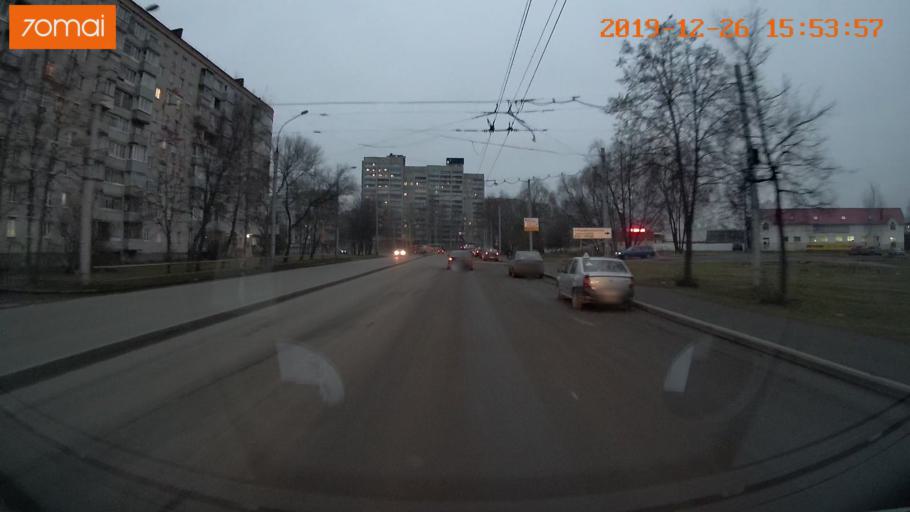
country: RU
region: Jaroslavl
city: Rybinsk
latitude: 58.0475
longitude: 38.8222
